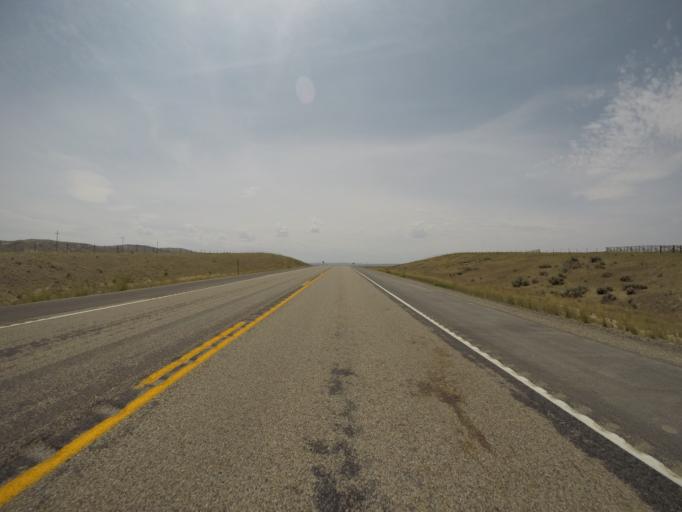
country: US
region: Wyoming
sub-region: Lincoln County
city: Kemmerer
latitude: 41.6950
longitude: -110.5667
